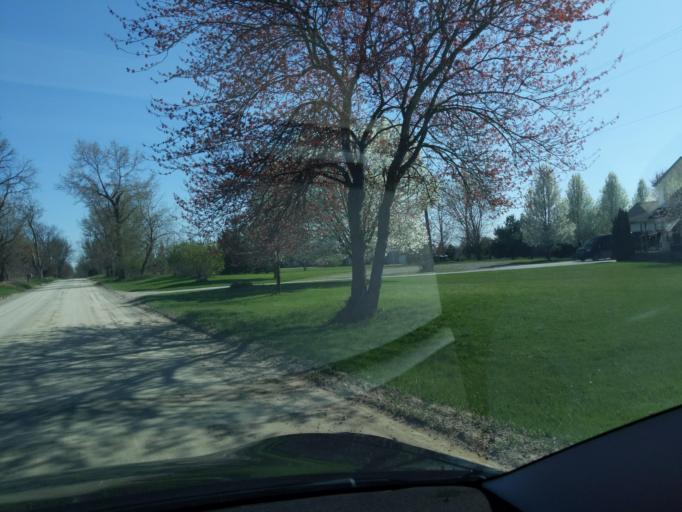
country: US
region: Michigan
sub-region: Ingham County
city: Stockbridge
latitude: 42.4239
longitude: -84.0836
